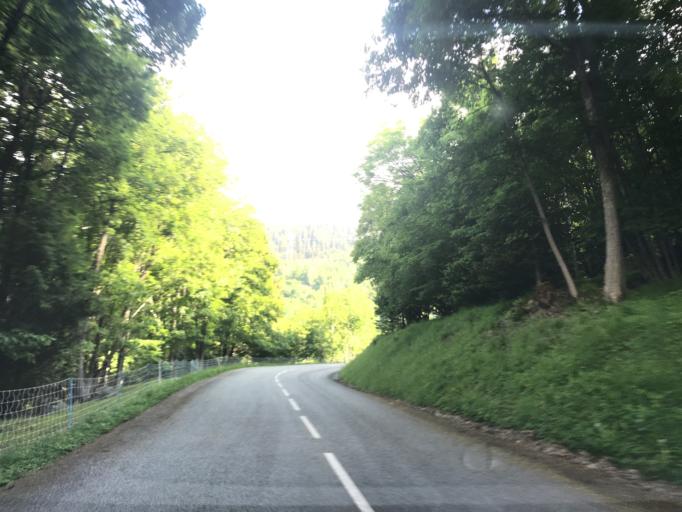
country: FR
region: Rhone-Alpes
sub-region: Departement de la Savoie
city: Modane
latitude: 45.2058
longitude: 6.6374
